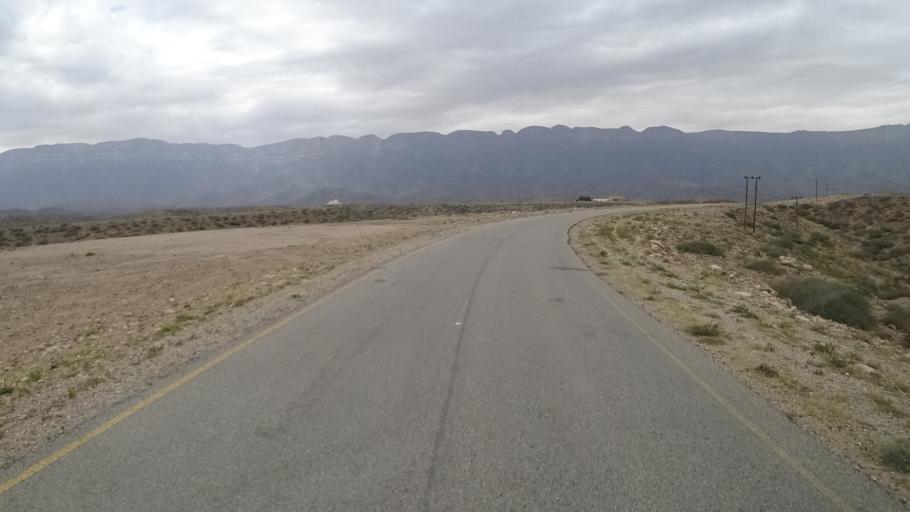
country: OM
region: Zufar
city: Salalah
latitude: 17.1471
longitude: 55.0052
